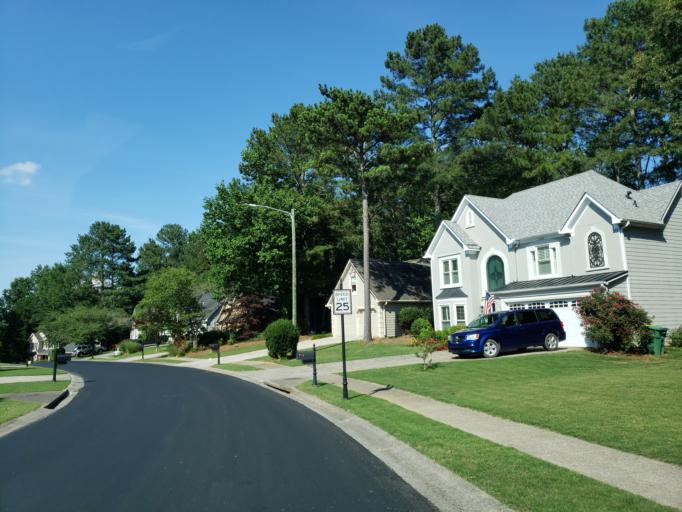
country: US
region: Georgia
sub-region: Cherokee County
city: Woodstock
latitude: 34.1167
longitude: -84.5338
